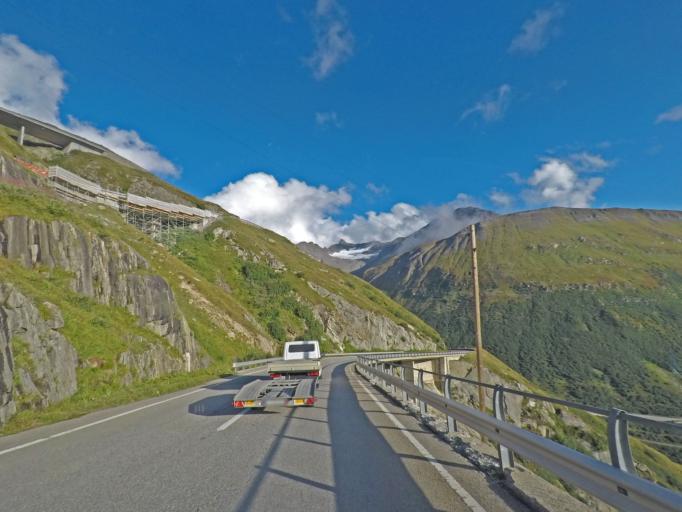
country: IT
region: Piedmont
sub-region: Provincia Verbano-Cusio-Ossola
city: Formazza
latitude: 46.5757
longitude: 8.3876
